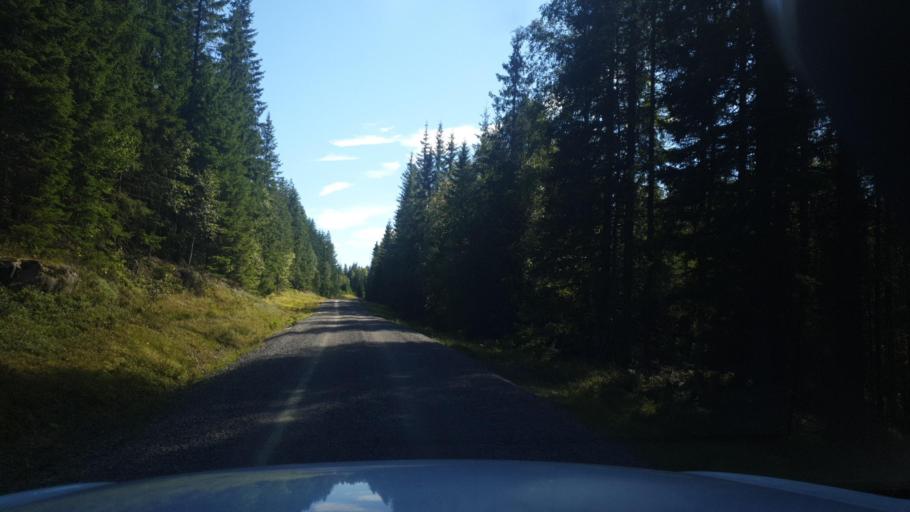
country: SE
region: Vaermland
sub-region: Eda Kommun
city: Charlottenberg
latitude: 60.0949
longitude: 12.6122
